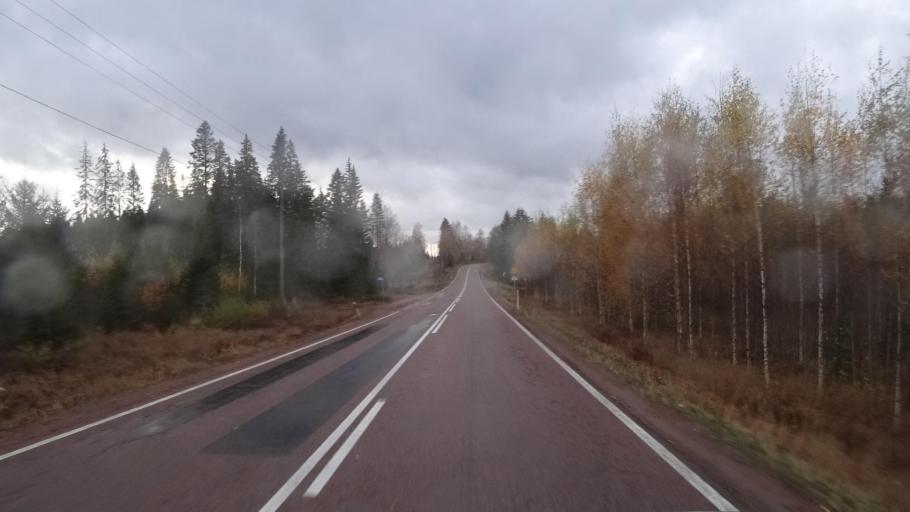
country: FI
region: Southern Savonia
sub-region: Mikkeli
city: Kangasniemi
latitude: 62.0944
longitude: 26.7268
